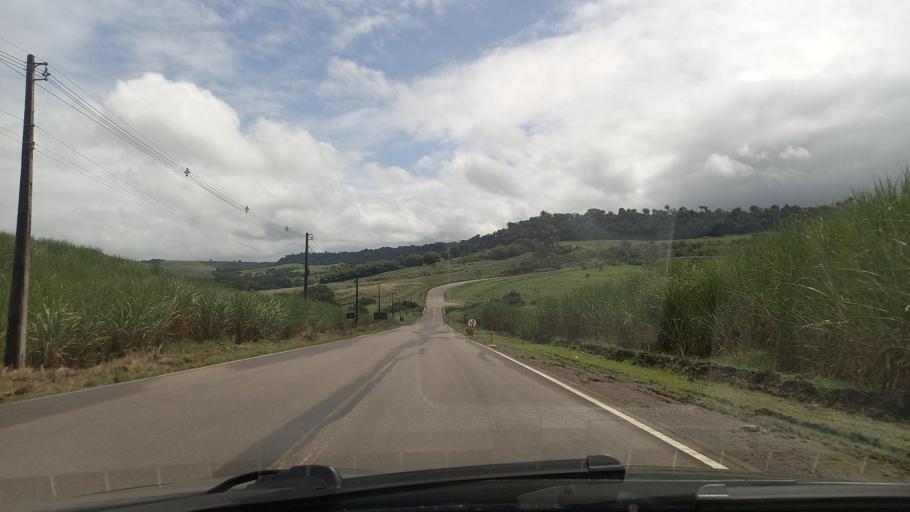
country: BR
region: Alagoas
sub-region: Sao Miguel Dos Campos
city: Sao Miguel dos Campos
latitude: -9.8169
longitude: -36.2199
